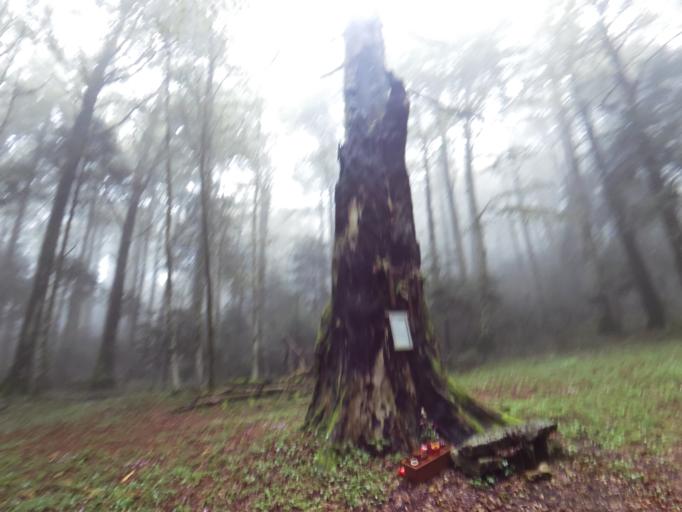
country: IT
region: Calabria
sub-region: Provincia di Vibo-Valentia
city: Mongiana
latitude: 38.5408
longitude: 16.3551
